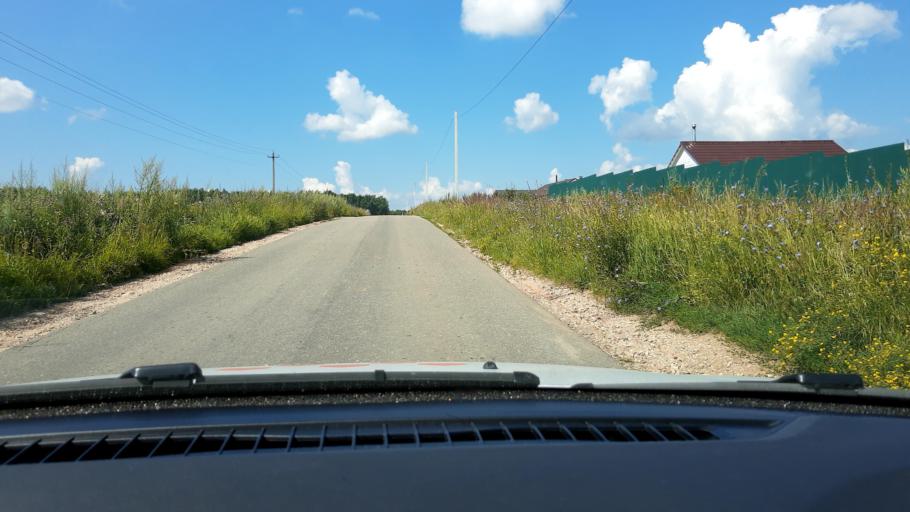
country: RU
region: Nizjnij Novgorod
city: Burevestnik
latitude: 56.0516
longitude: 43.9601
